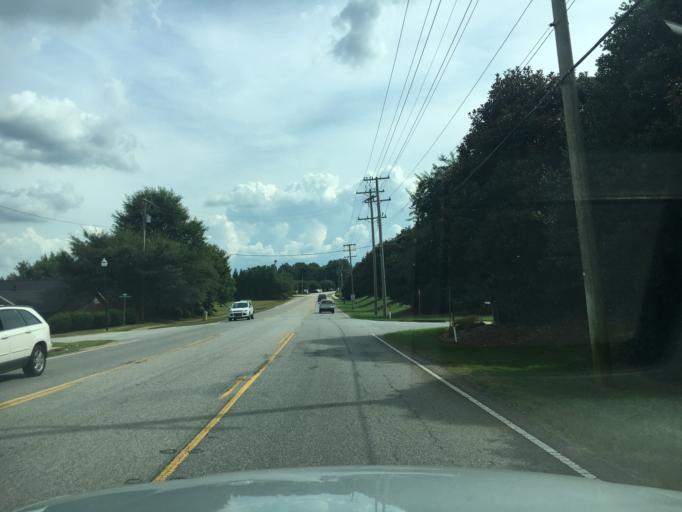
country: US
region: South Carolina
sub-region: Greenville County
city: Greer
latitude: 34.8915
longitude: -82.2421
